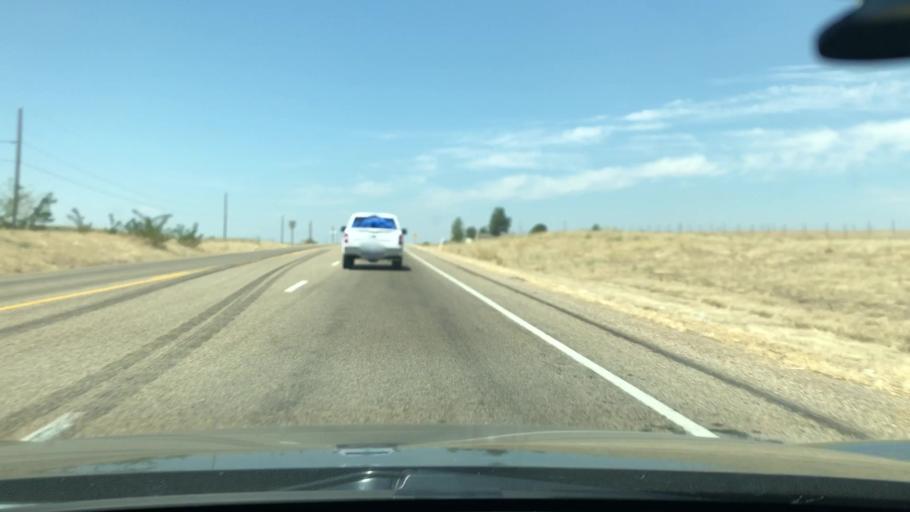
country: US
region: Idaho
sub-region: Canyon County
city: Parma
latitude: 43.8221
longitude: -116.9545
